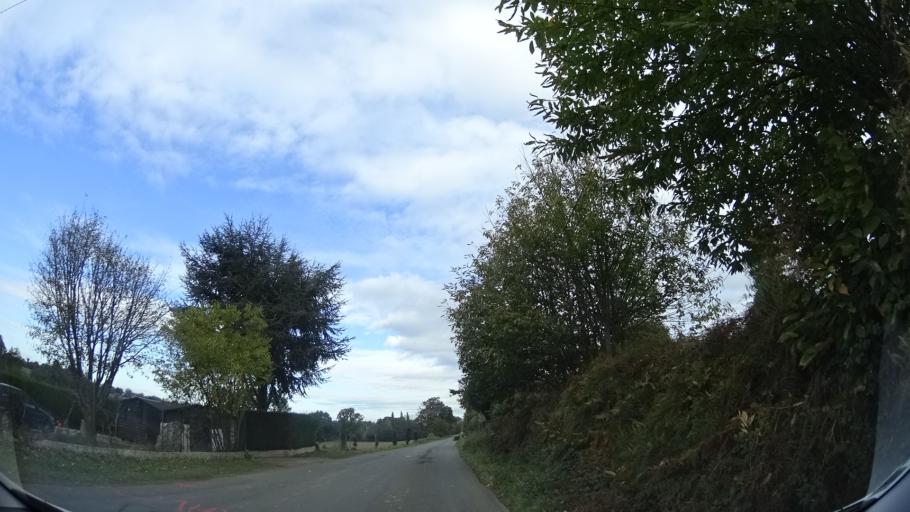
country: FR
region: Brittany
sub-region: Departement d'Ille-et-Vilaine
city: Vignoc
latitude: 48.2359
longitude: -1.7885
